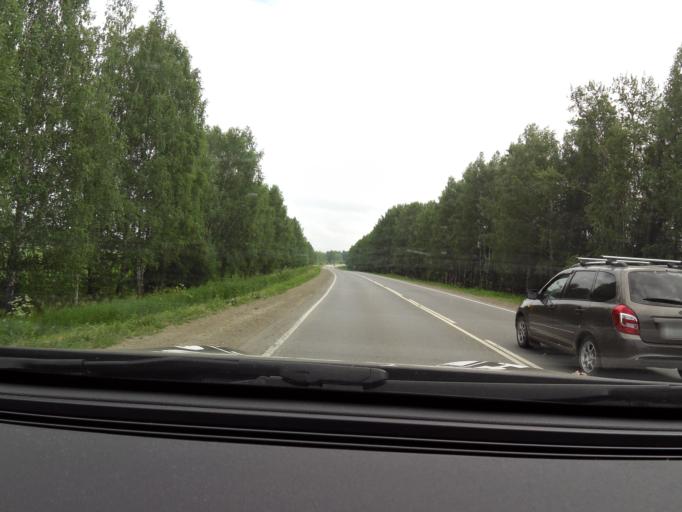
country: RU
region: Perm
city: Kukushtan
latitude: 57.4832
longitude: 56.6812
